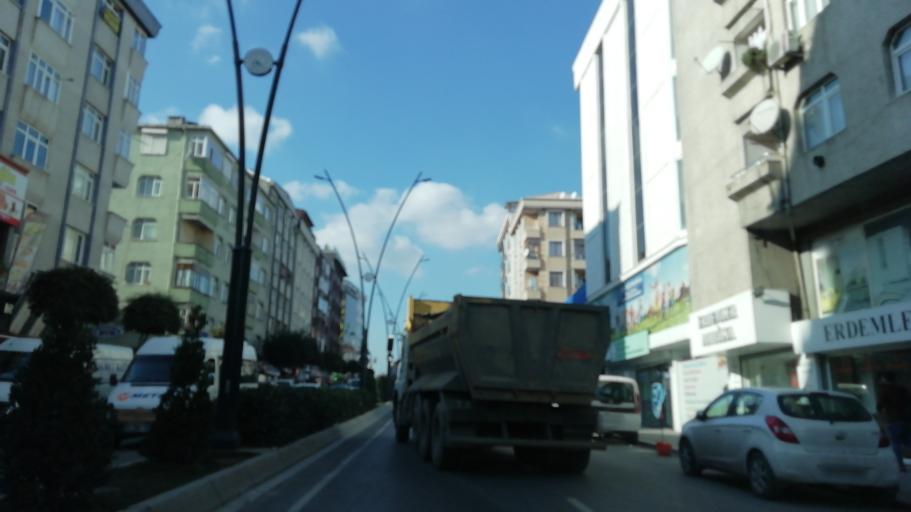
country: TR
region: Istanbul
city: Esenler
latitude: 41.0579
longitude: 28.9192
